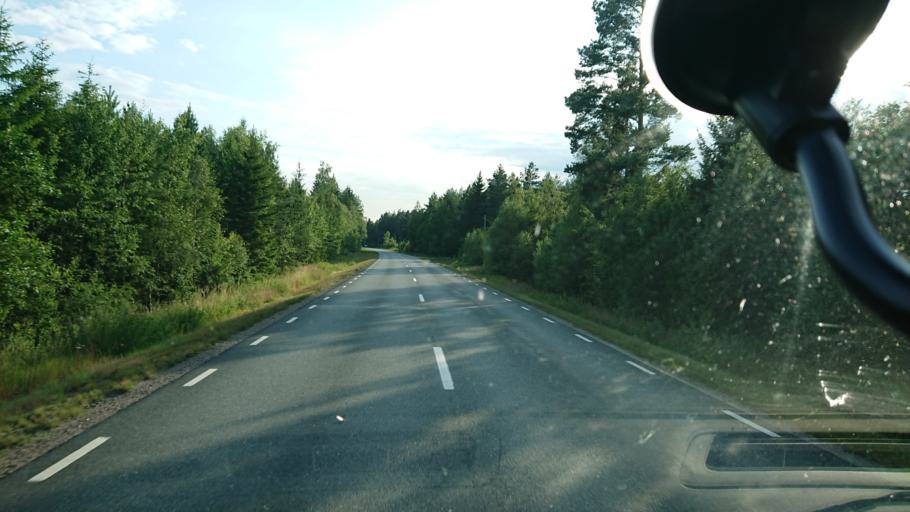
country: SE
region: Kronoberg
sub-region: Vaxjo Kommun
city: Rottne
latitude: 57.0360
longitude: 14.9073
